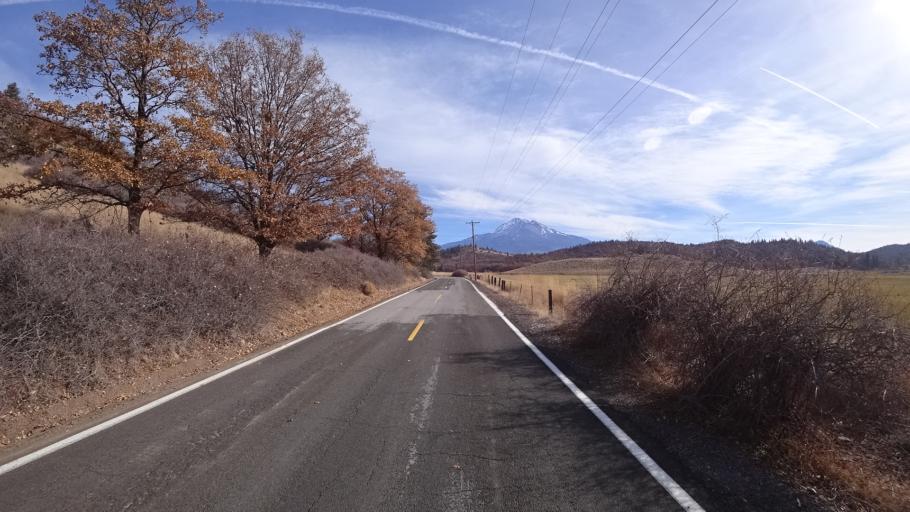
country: US
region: California
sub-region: Siskiyou County
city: Weed
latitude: 41.4673
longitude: -122.4291
